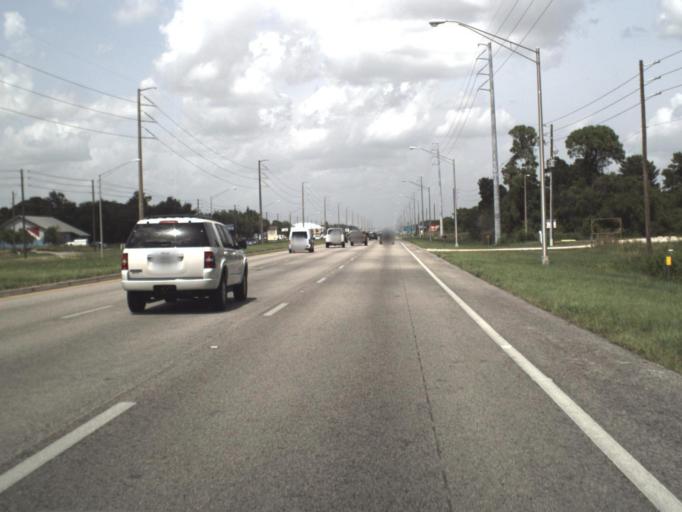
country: US
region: Florida
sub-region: Highlands County
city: Avon Park
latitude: 27.5311
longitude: -81.5009
